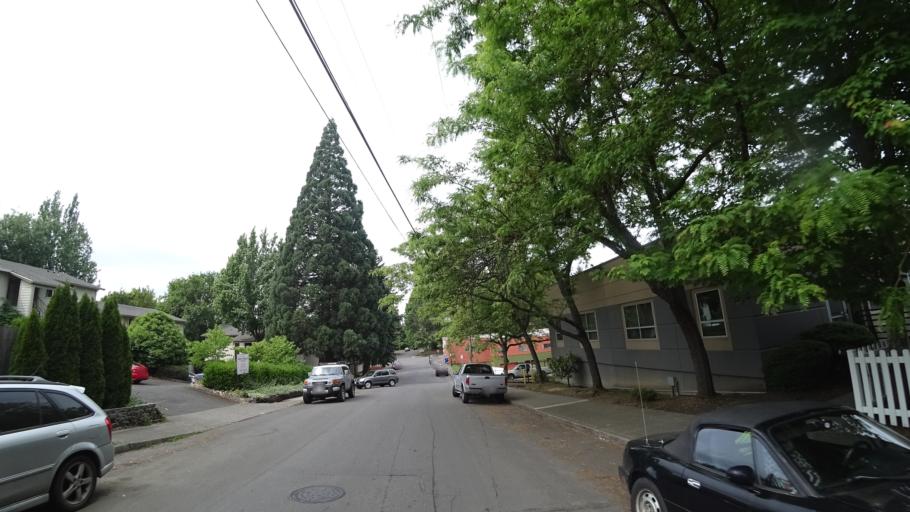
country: US
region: Oregon
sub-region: Clackamas County
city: Milwaukie
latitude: 45.4958
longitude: -122.6305
